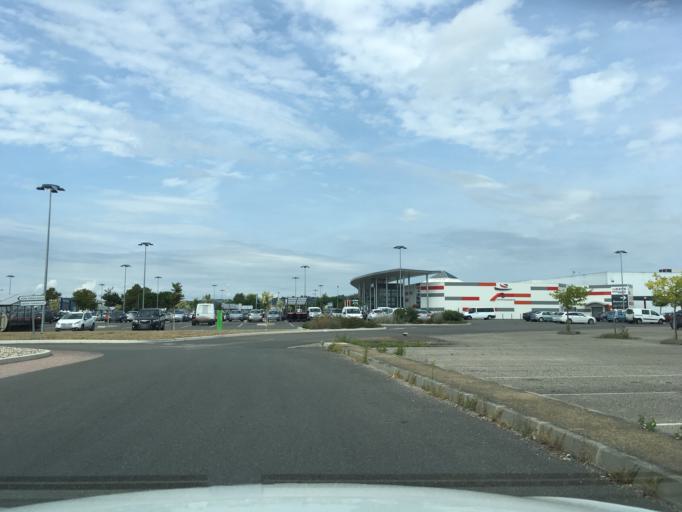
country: FR
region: Aquitaine
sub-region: Departement du Lot-et-Garonne
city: Boe
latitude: 44.1805
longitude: 0.6195
